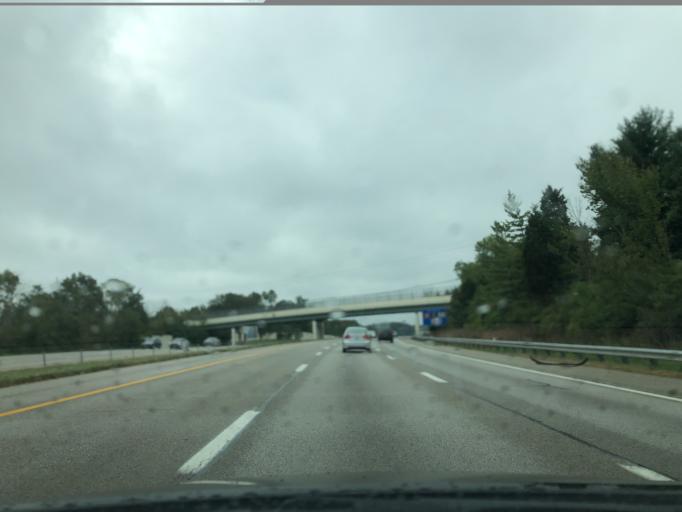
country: US
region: Ohio
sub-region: Hamilton County
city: The Village of Indian Hill
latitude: 39.2497
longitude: -84.3082
